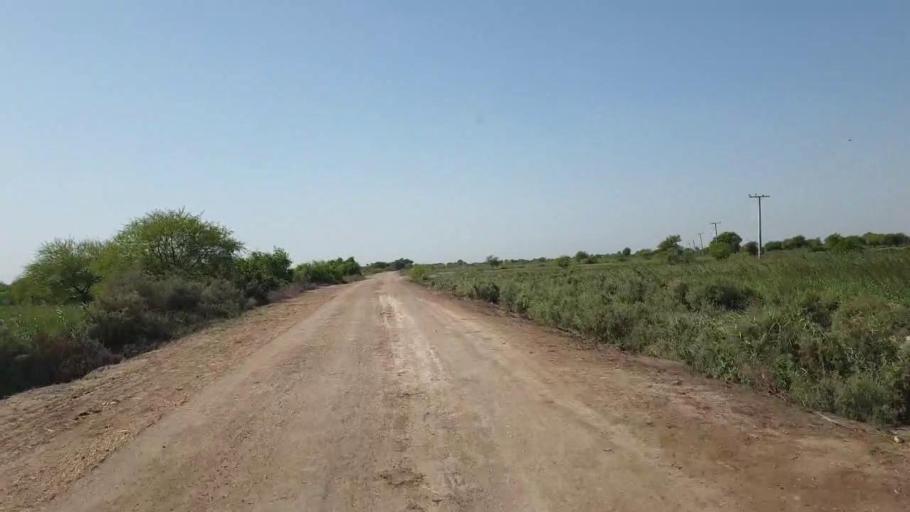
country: PK
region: Sindh
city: Tando Bago
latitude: 24.7048
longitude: 69.0361
